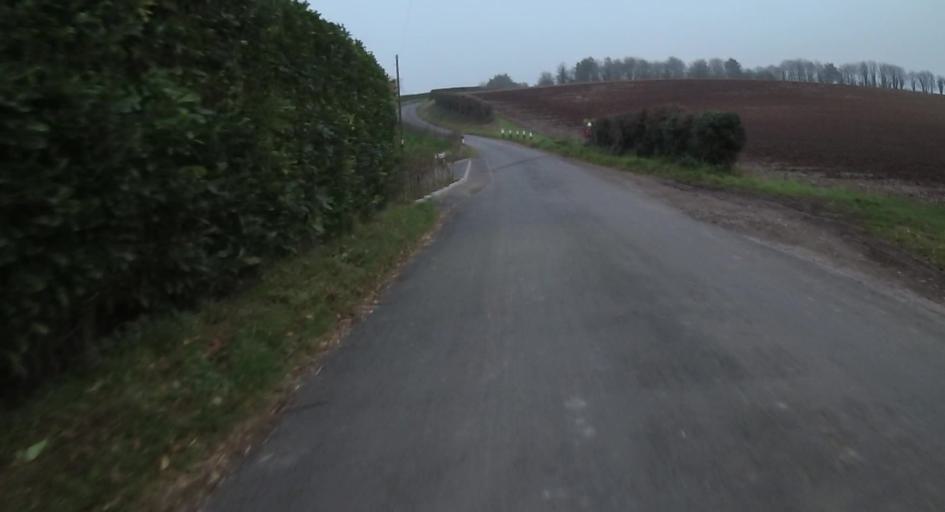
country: GB
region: England
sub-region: Hampshire
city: Kings Worthy
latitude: 51.0797
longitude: -1.2843
